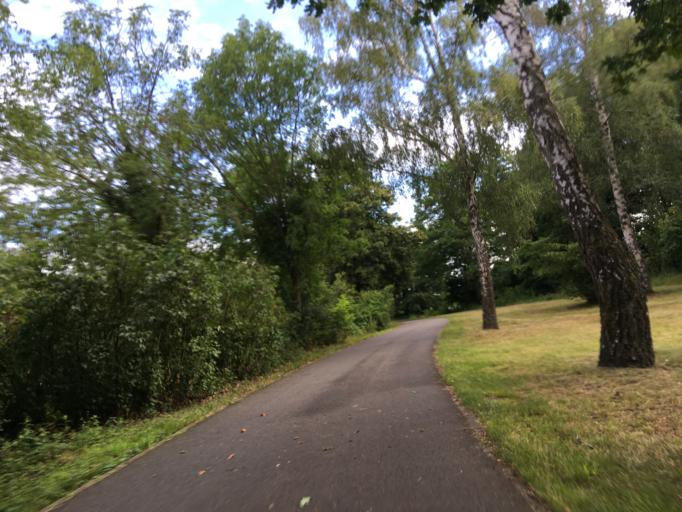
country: DE
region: Berlin
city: Konradshohe
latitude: 52.5794
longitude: 13.2163
